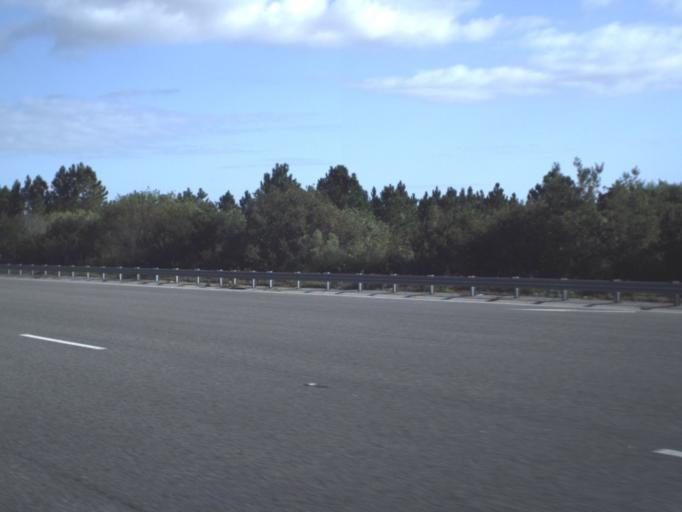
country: US
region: Florida
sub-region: Osceola County
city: Saint Cloud
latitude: 28.1871
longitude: -81.3041
